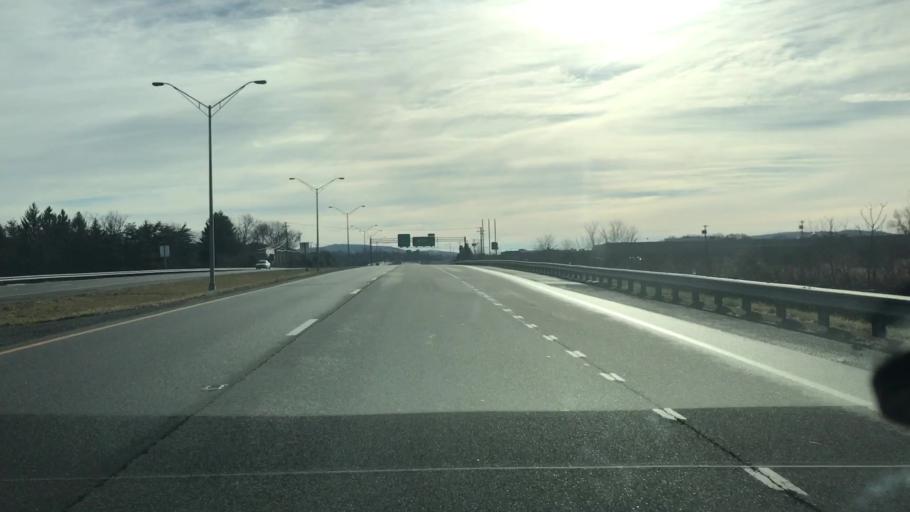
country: US
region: Virginia
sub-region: Montgomery County
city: Christiansburg
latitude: 37.1377
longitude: -80.3799
